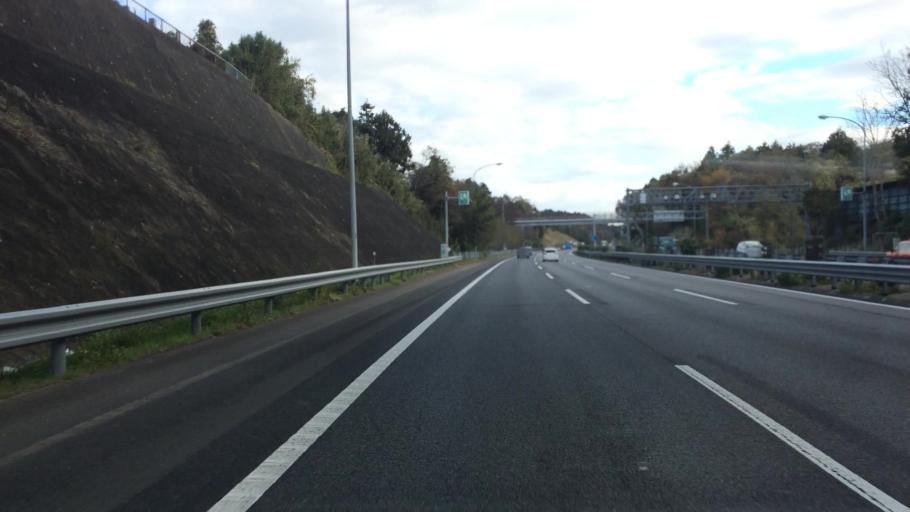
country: JP
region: Chiba
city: Shisui
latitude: 35.6967
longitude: 140.2564
